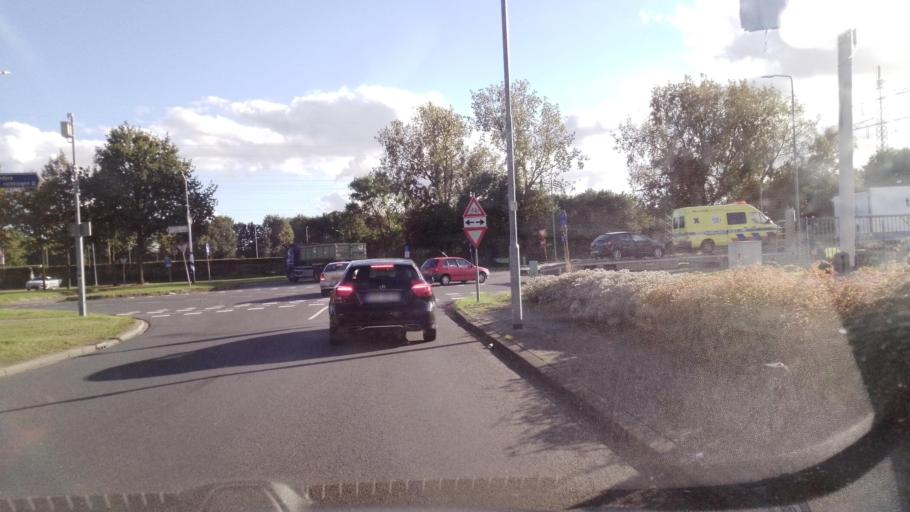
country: NL
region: Limburg
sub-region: Gemeente Venlo
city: Venlo
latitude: 51.3818
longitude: 6.1407
